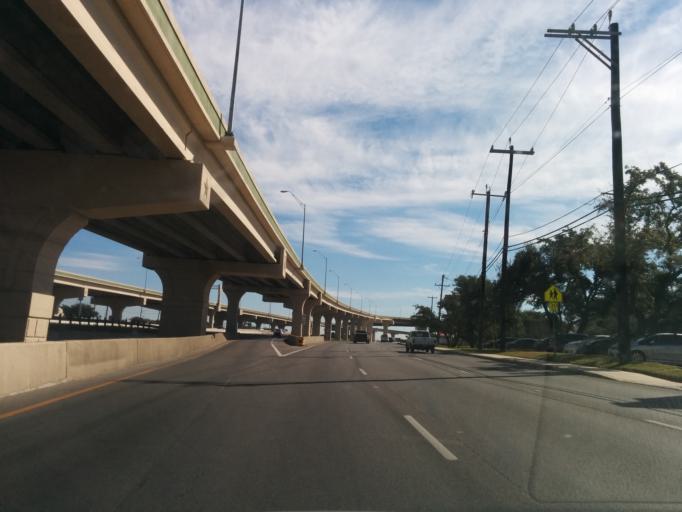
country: US
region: Texas
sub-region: Bexar County
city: Hollywood Park
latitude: 29.6100
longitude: -98.4745
